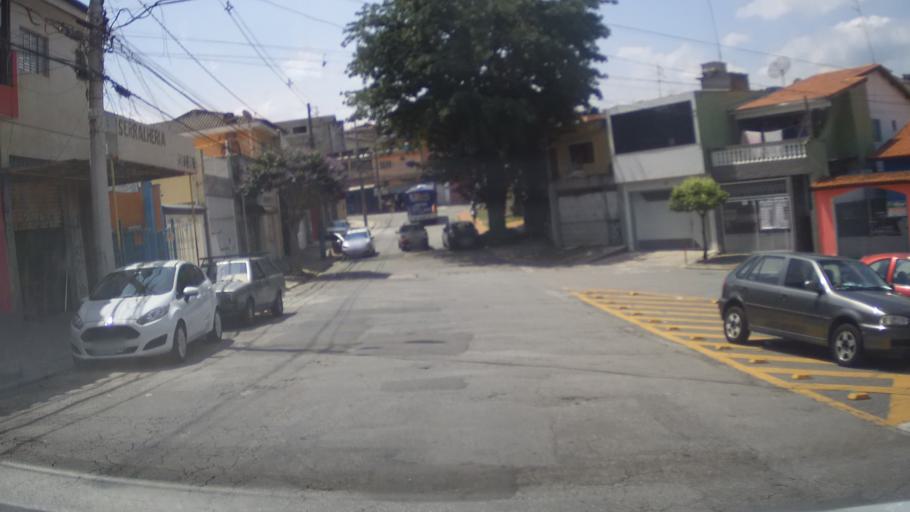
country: BR
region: Sao Paulo
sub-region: Guarulhos
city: Guarulhos
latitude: -23.4271
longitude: -46.5283
